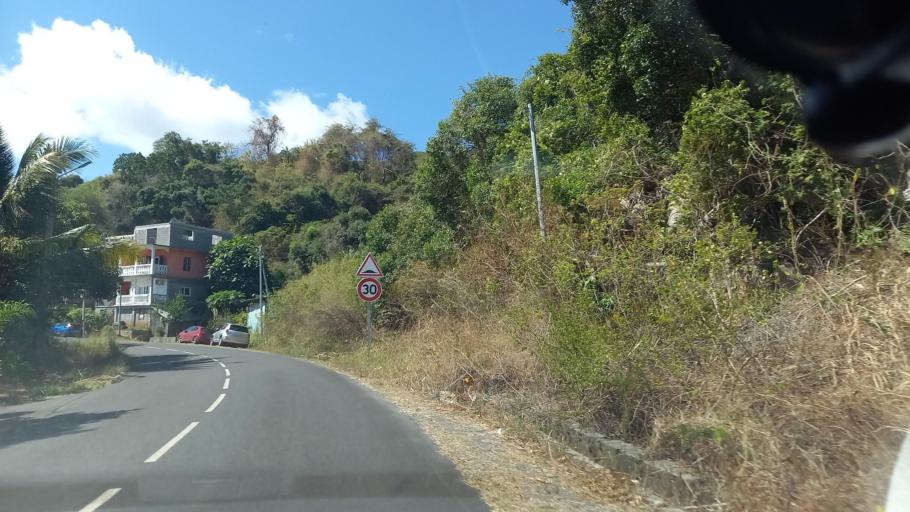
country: YT
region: Kani-Keli
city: Kani Keli
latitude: -12.9460
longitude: 45.1013
